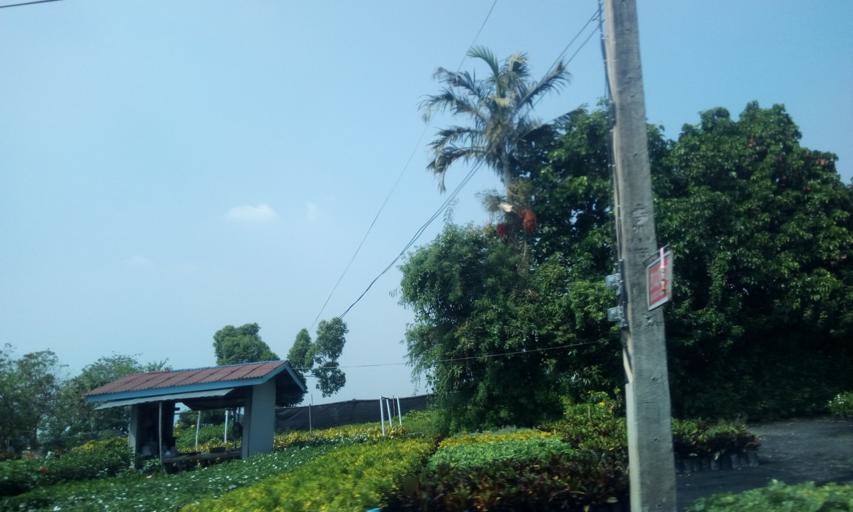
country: TH
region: Nakhon Nayok
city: Ongkharak
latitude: 14.1397
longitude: 100.9705
